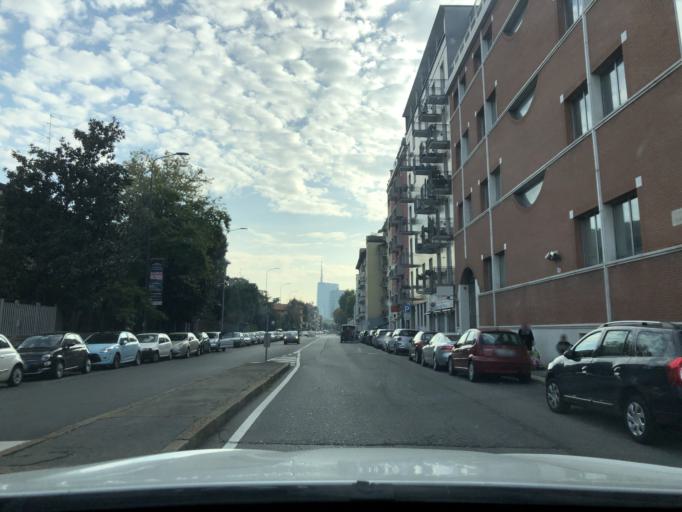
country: IT
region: Lombardy
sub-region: Citta metropolitana di Milano
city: Milano
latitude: 45.4987
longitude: 9.1982
